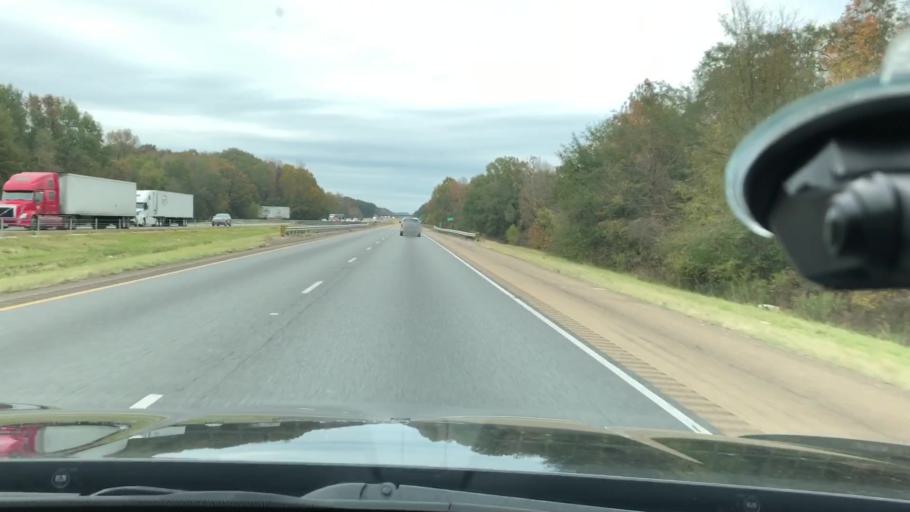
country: US
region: Arkansas
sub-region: Nevada County
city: Prescott
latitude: 33.8961
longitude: -93.3067
